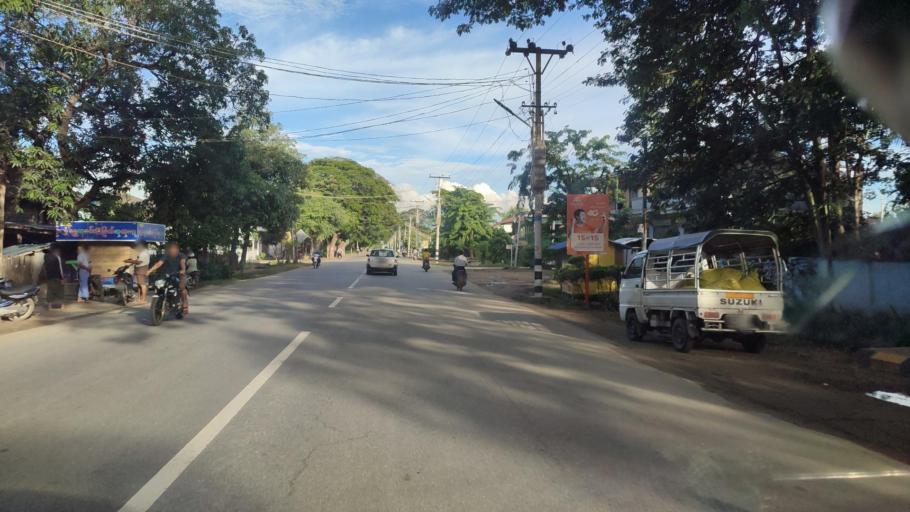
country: MM
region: Mandalay
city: Yamethin
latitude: 20.1282
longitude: 96.2032
